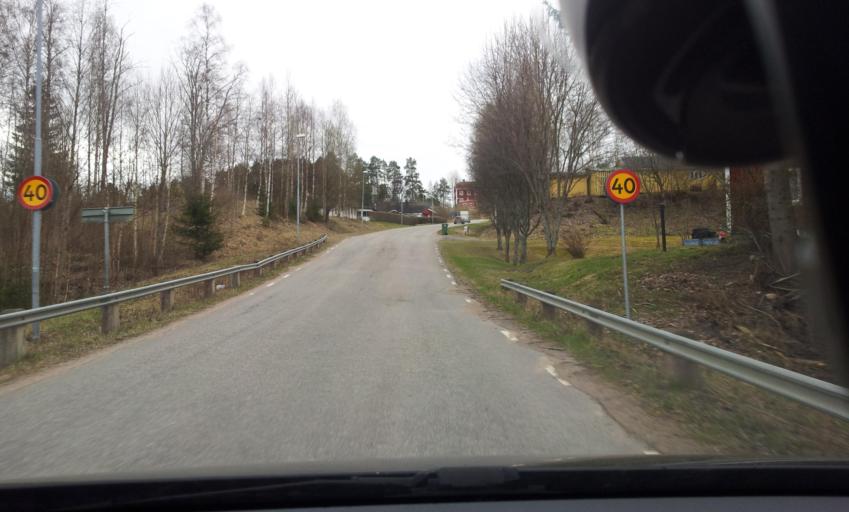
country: SE
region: Gaevleborg
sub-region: Ljusdals Kommun
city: Farila
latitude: 61.8042
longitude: 15.8501
